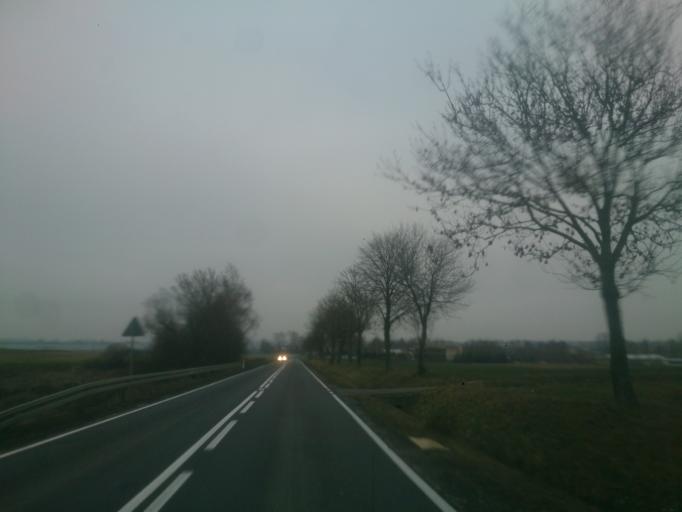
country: PL
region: Warmian-Masurian Voivodeship
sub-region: Powiat ilawski
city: Lubawa
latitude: 53.5047
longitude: 19.7077
